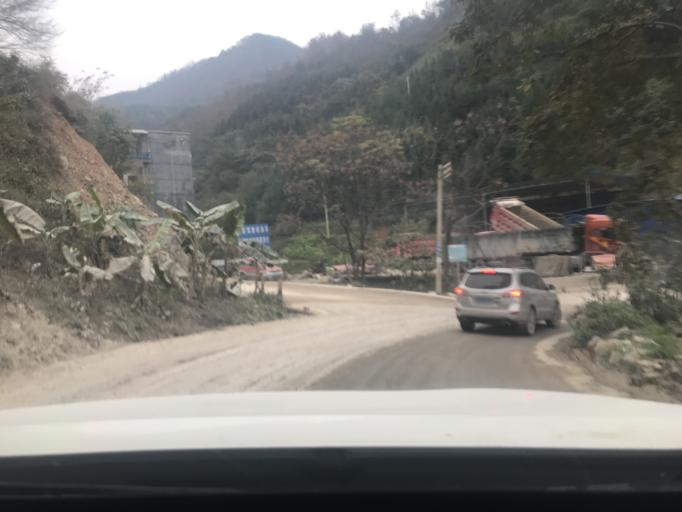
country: CN
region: Guangxi Zhuangzu Zizhiqu
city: Xinzhou
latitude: 24.9850
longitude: 105.8219
